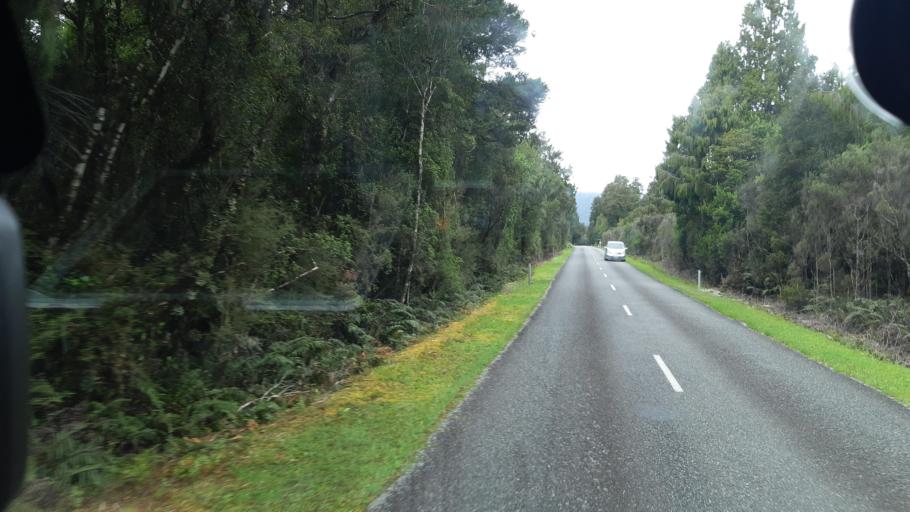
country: NZ
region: West Coast
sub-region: Westland District
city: Hokitika
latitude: -42.7837
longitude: 171.1154
